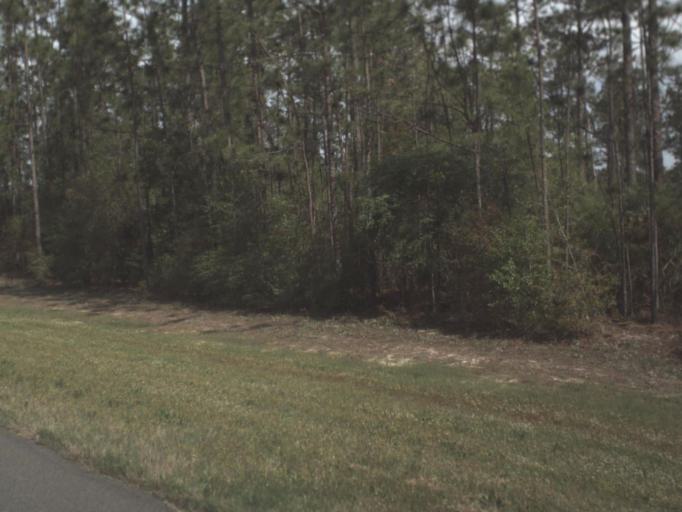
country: US
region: Florida
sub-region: Santa Rosa County
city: East Milton
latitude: 30.6873
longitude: -86.8231
